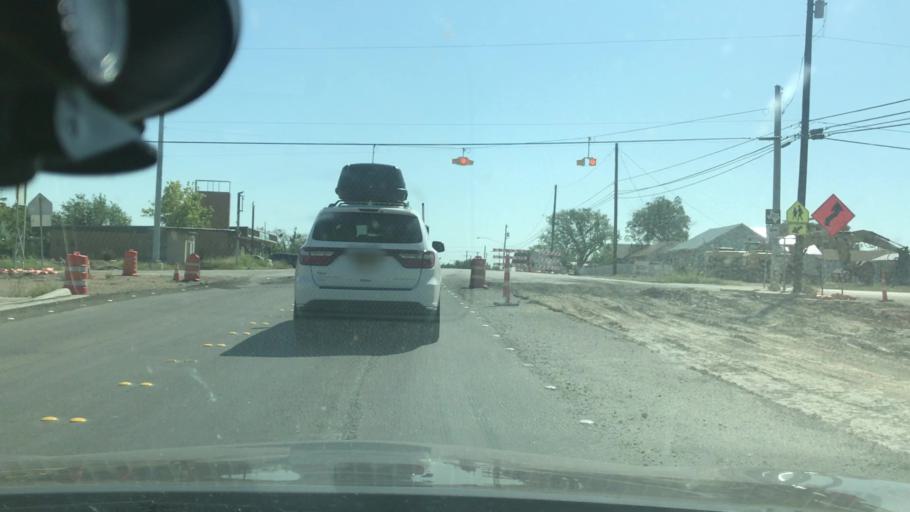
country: US
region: Texas
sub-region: Stephens County
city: Breckenridge
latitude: 32.7555
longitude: -98.8857
